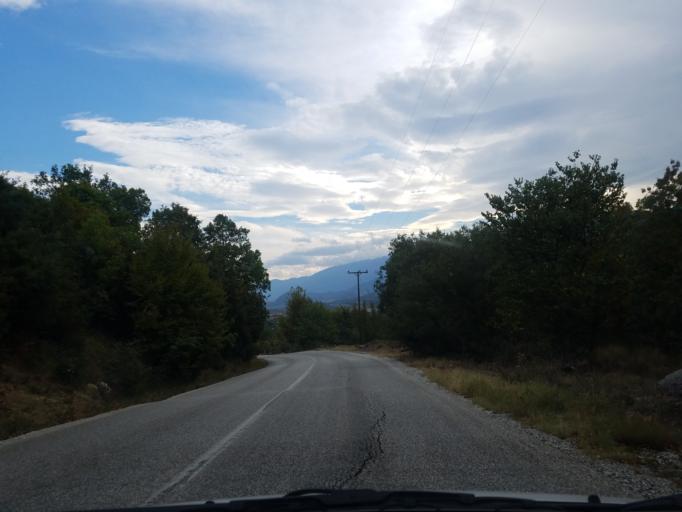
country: GR
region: Thessaly
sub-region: Trikala
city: Kalampaka
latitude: 39.7006
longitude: 21.6495
